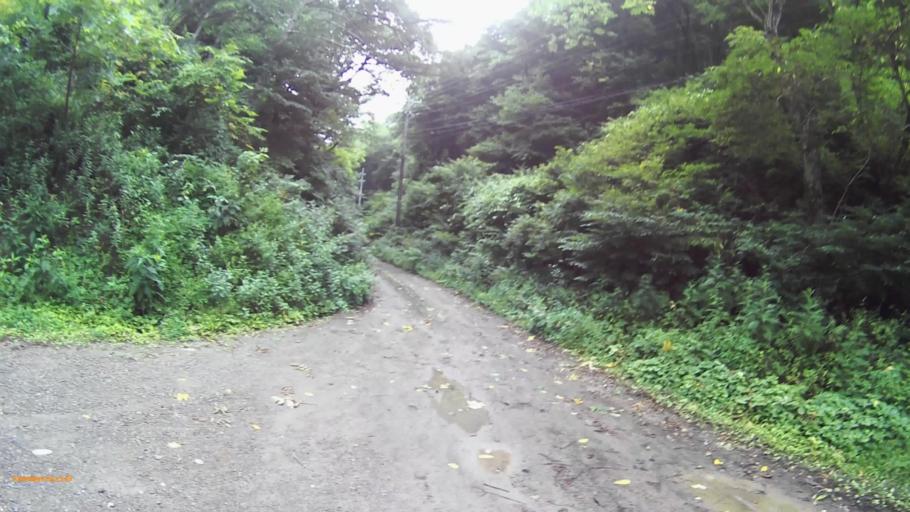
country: JP
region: Nagano
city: Ina
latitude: 35.9517
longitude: 137.7961
